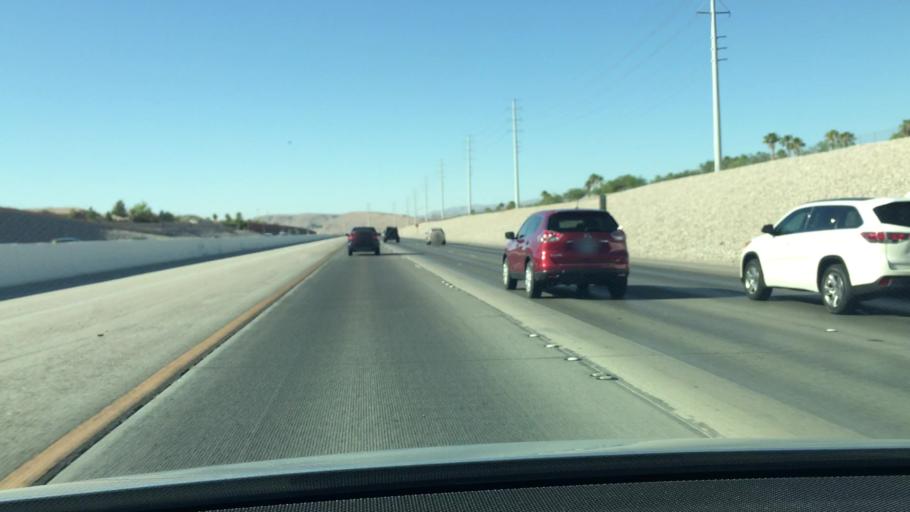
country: US
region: Nevada
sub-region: Clark County
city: Summerlin South
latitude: 36.1440
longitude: -115.3368
